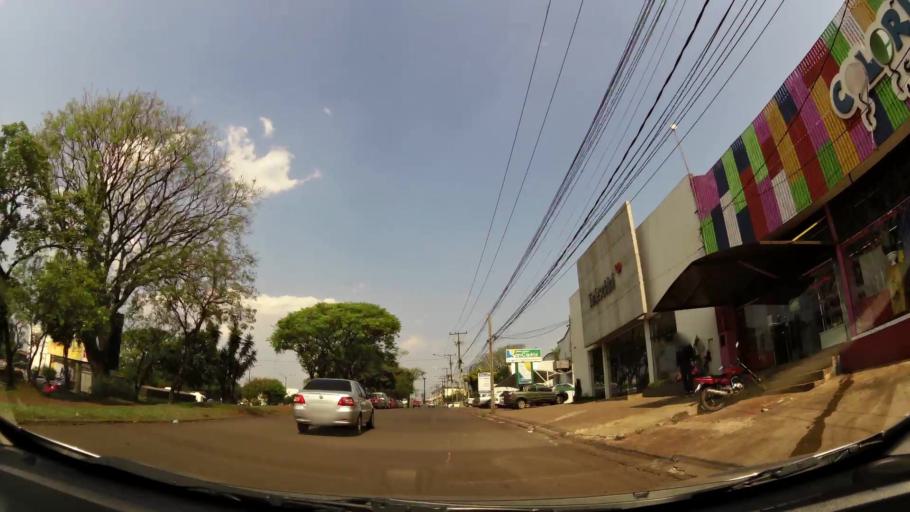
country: PY
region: Alto Parana
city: Ciudad del Este
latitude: -25.5106
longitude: -54.6287
